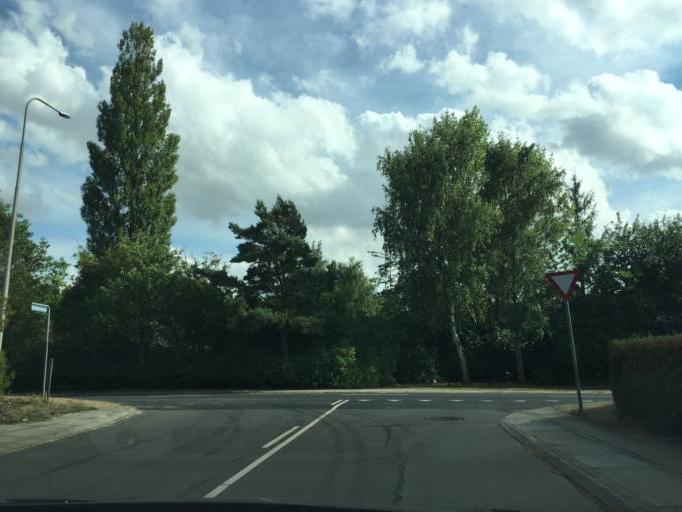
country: DK
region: South Denmark
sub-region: Odense Kommune
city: Odense
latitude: 55.3500
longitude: 10.3841
